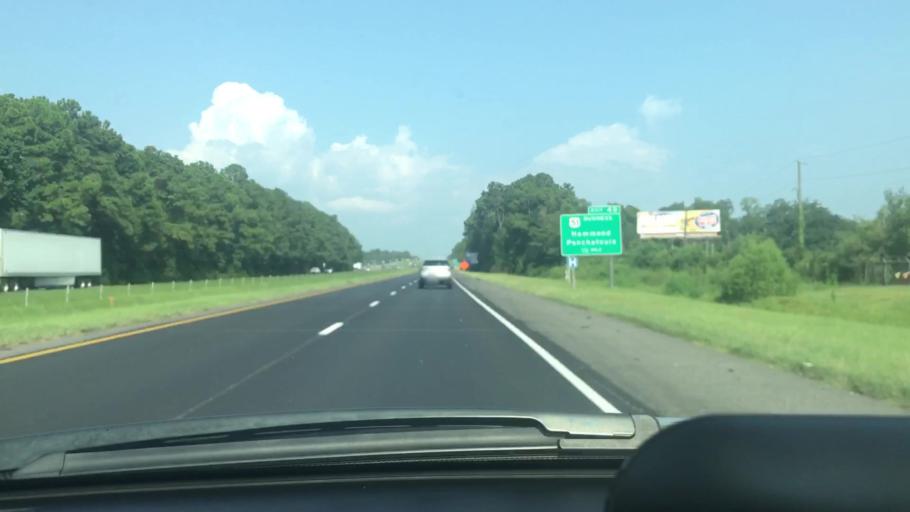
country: US
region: Louisiana
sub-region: Tangipahoa Parish
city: Hammond
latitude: 30.4788
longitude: -90.4689
